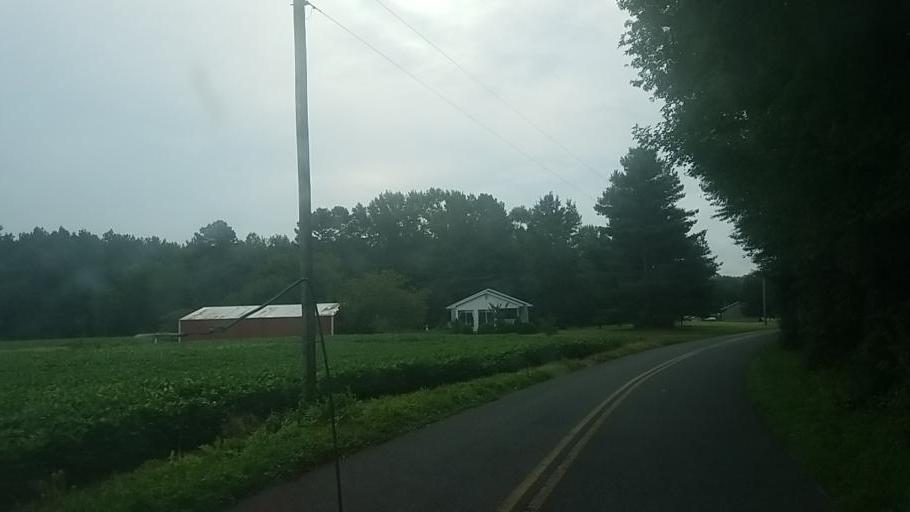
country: US
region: Delaware
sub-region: Sussex County
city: Selbyville
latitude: 38.4248
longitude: -75.2894
